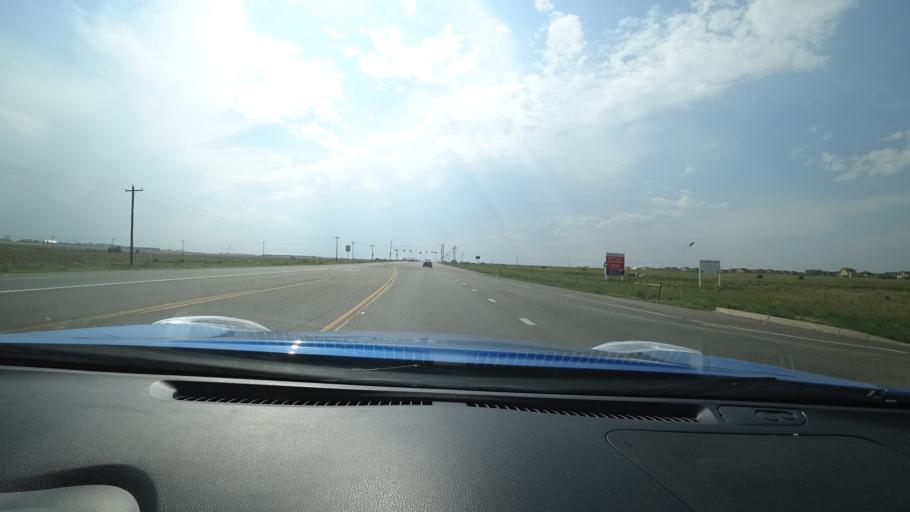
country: US
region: Colorado
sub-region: Boulder County
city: Erie
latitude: 40.0005
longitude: -105.0014
